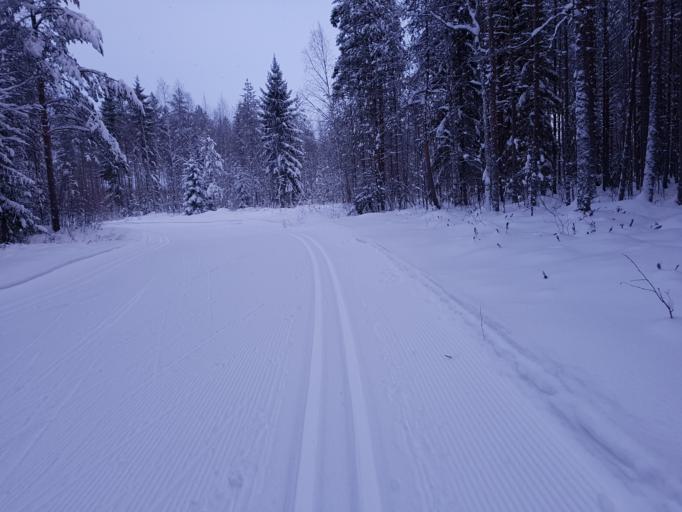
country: FI
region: Kainuu
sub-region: Kehys-Kainuu
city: Kuhmo
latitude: 64.1134
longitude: 29.5665
